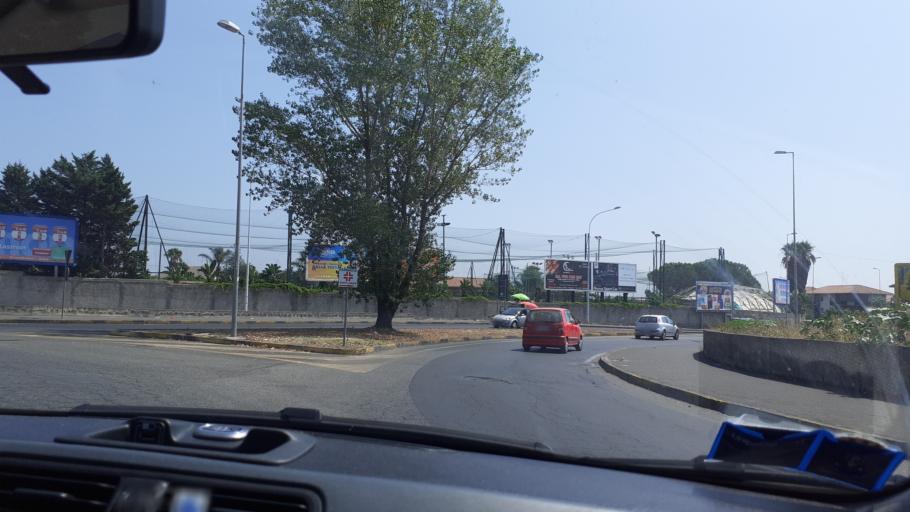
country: IT
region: Sicily
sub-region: Catania
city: Misterbianco
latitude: 37.5140
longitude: 15.0534
